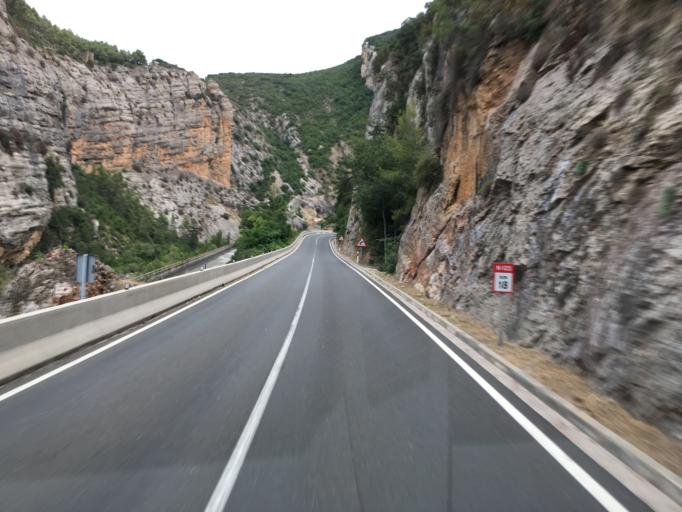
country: ES
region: Aragon
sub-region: Provincia de Huesca
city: Estada
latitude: 42.1050
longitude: 0.2823
